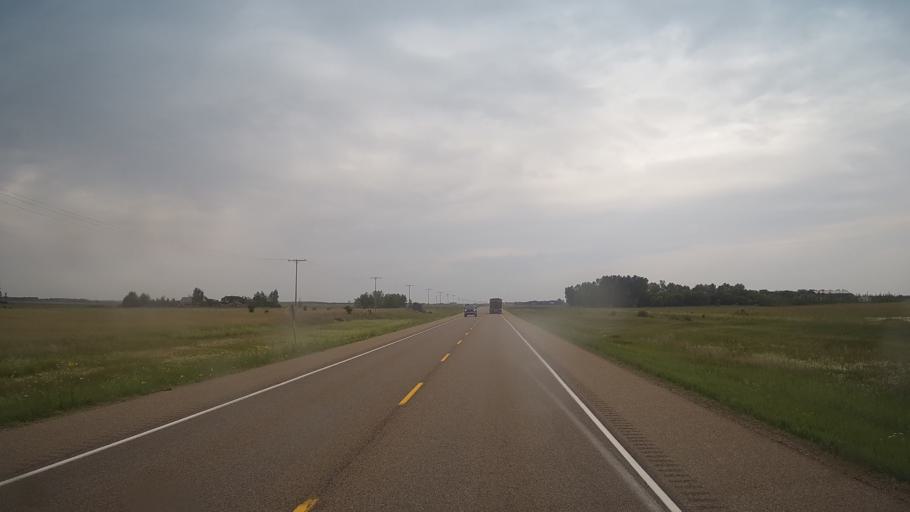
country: CA
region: Saskatchewan
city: Langham
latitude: 52.1289
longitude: -107.1371
